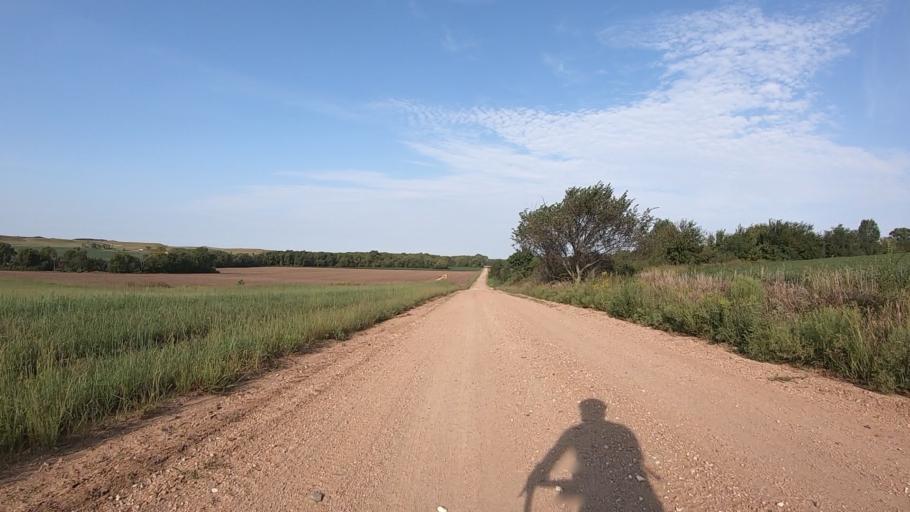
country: US
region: Kansas
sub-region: Marshall County
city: Blue Rapids
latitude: 39.6570
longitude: -96.8706
